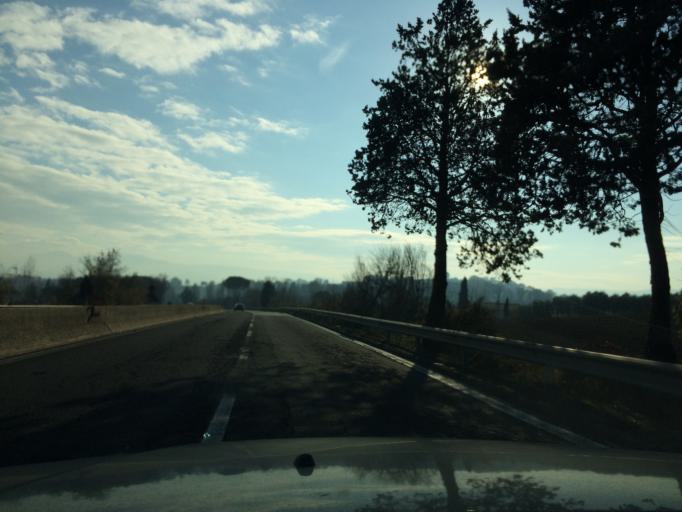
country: IT
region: Umbria
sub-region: Provincia di Terni
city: San Gemini
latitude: 42.5964
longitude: 12.5631
